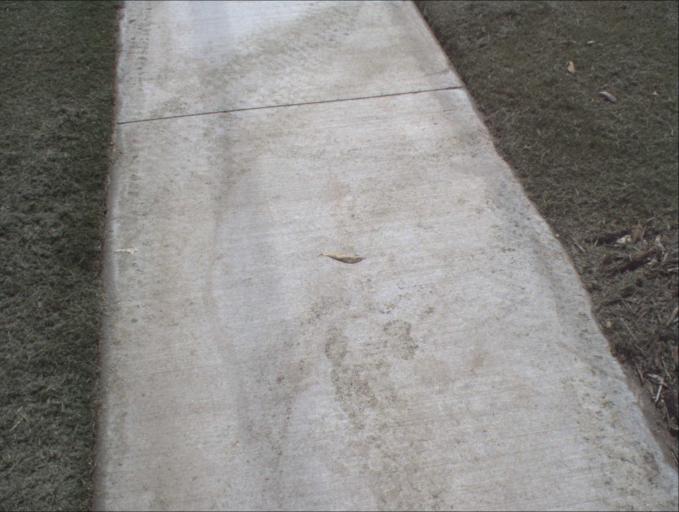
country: AU
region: Queensland
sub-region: Logan
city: Waterford West
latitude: -27.6843
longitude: 153.1580
